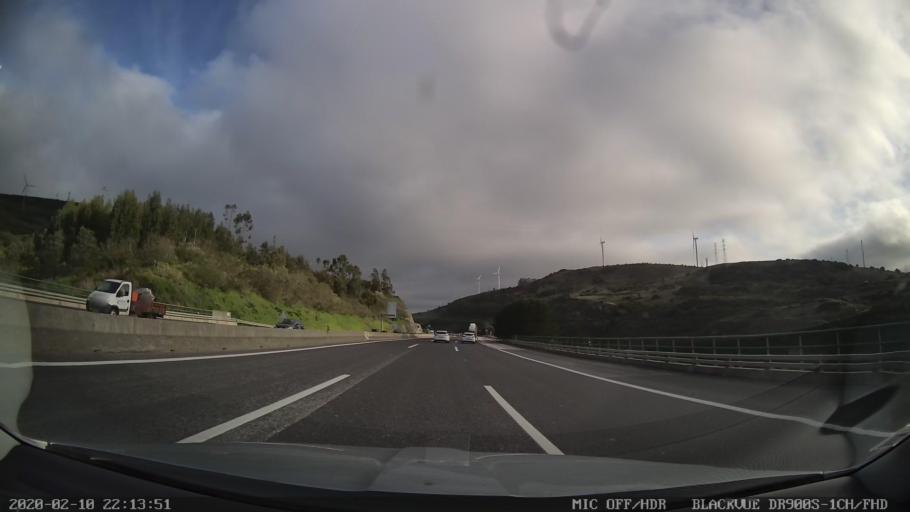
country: PT
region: Lisbon
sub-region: Loures
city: Santo Antao do Tojal
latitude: 38.8757
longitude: -9.1321
